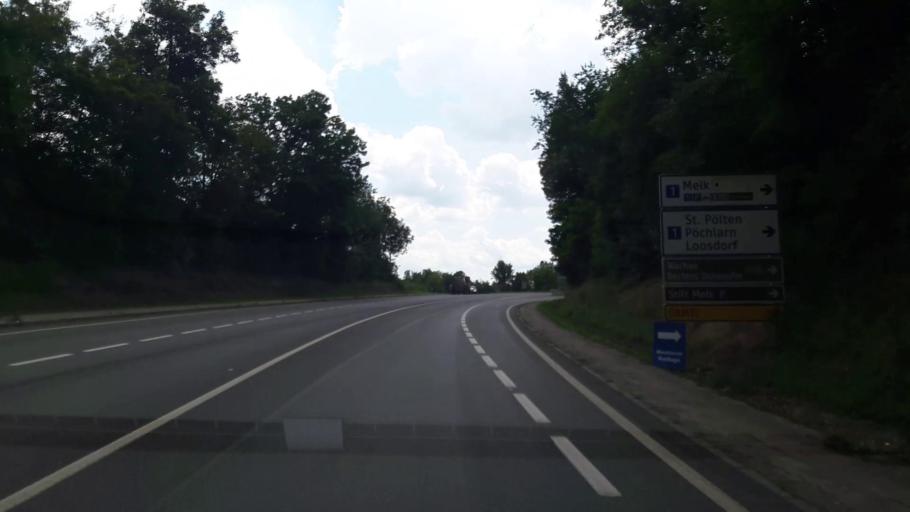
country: AT
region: Lower Austria
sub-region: Politischer Bezirk Melk
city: Emmersdorf an der Donau
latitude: 48.2370
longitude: 15.3490
